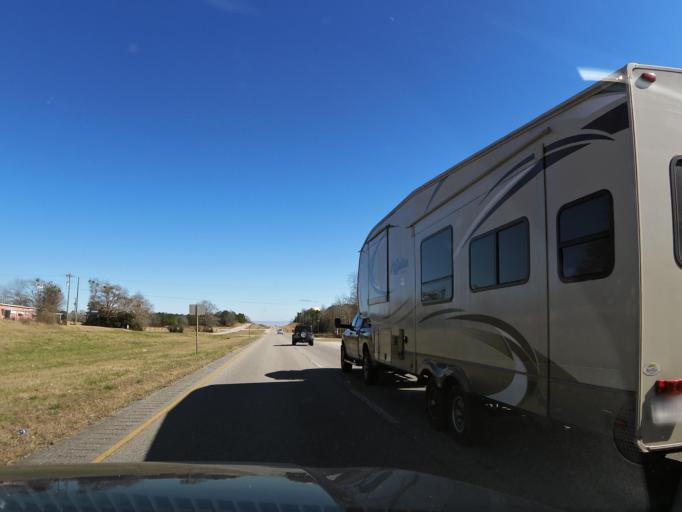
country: US
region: Alabama
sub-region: Bullock County
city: Union Springs
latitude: 32.1461
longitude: -85.6910
